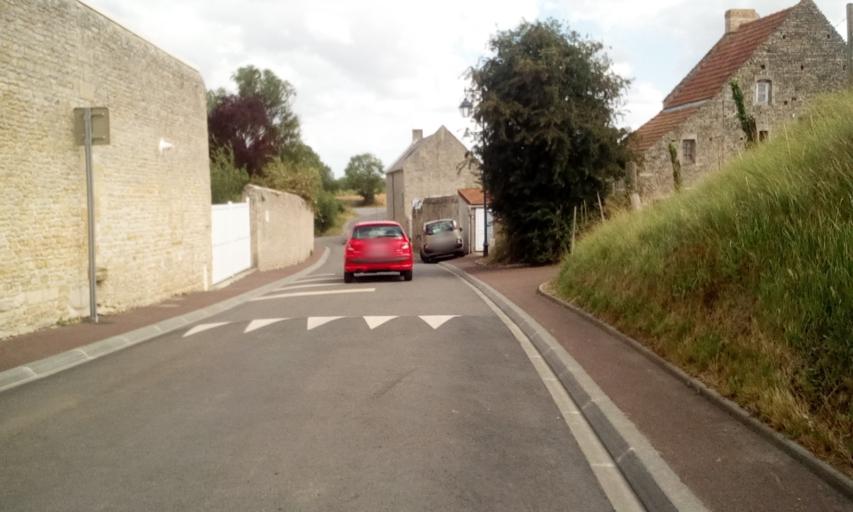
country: FR
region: Lower Normandy
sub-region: Departement du Calvados
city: Courseulles-sur-Mer
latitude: 49.3110
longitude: -0.4823
